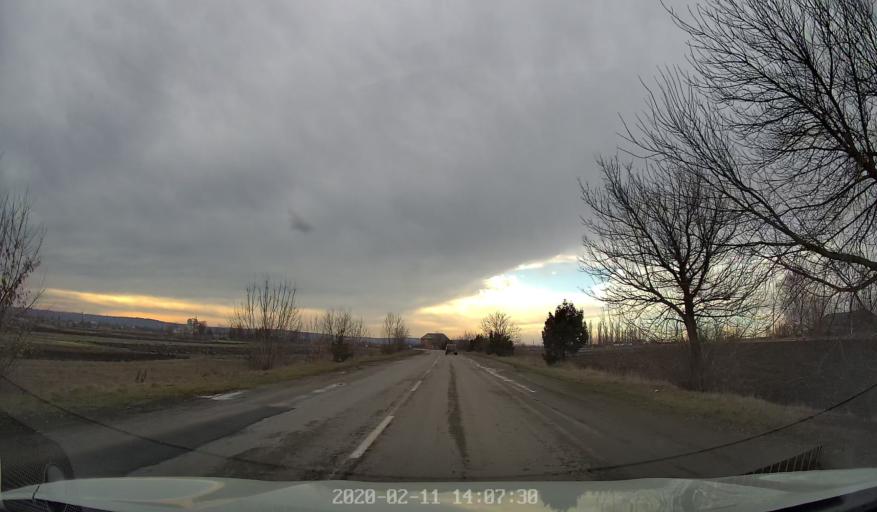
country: RO
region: Botosani
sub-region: Comuna Darabani
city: Bajura
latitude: 48.2463
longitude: 26.5531
